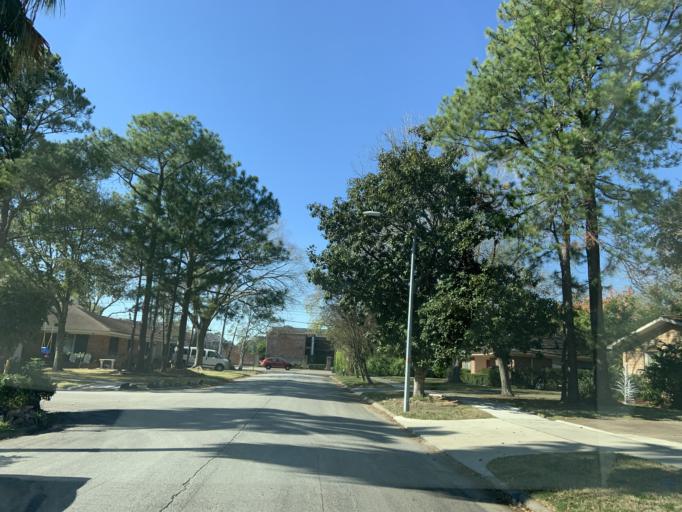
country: US
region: Texas
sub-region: Harris County
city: Bellaire
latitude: 29.6816
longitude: -95.5078
